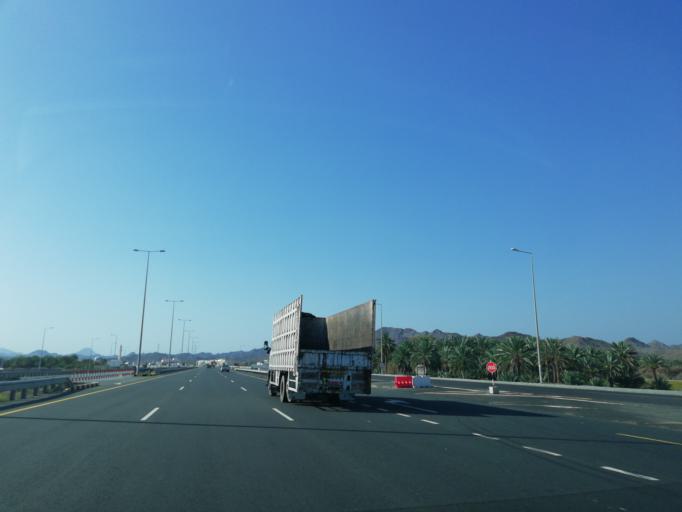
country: OM
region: Muhafazat ad Dakhiliyah
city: Sufalat Sama'il
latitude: 23.0307
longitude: 58.2053
